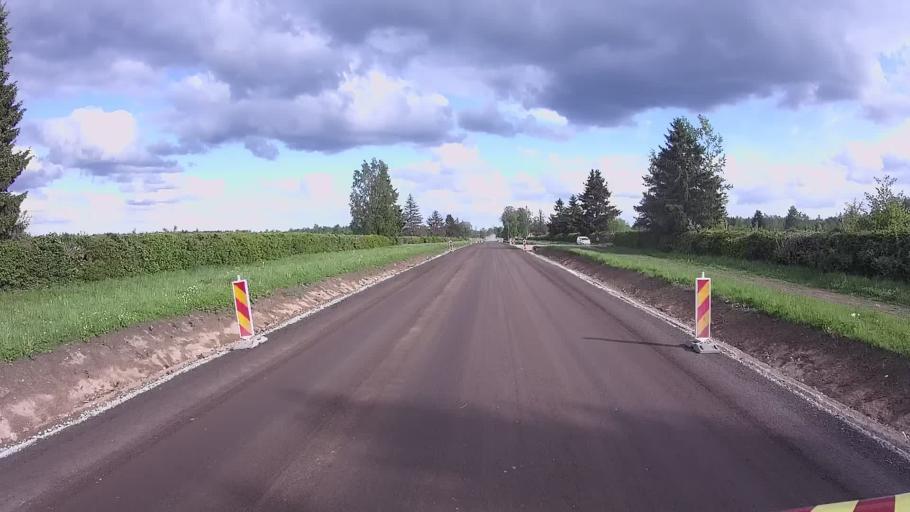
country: EE
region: Jogevamaa
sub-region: Mustvee linn
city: Mustvee
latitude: 59.0217
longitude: 26.7008
